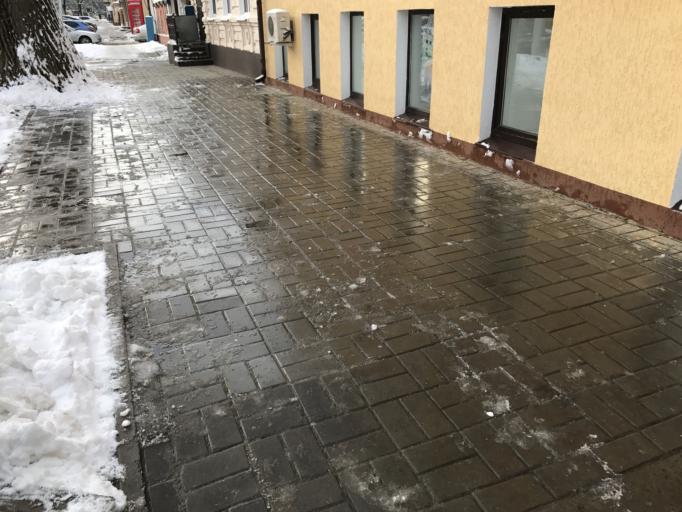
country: RU
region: Stavropol'skiy
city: Stavropol'
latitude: 45.0465
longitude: 41.9668
